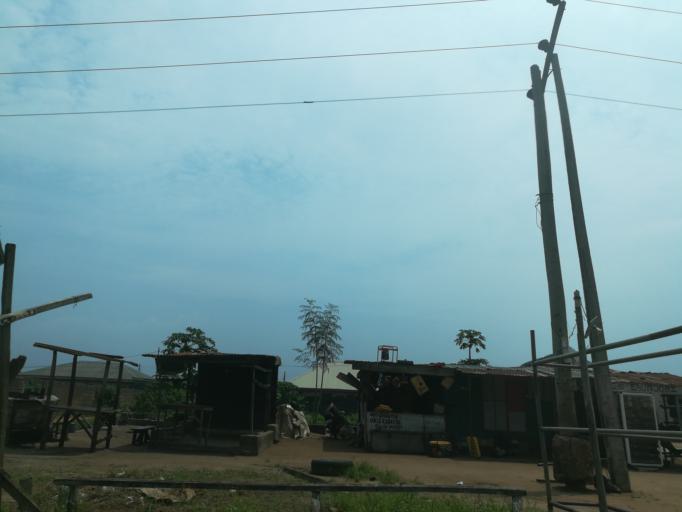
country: NG
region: Lagos
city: Ikorodu
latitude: 6.6065
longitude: 3.5961
